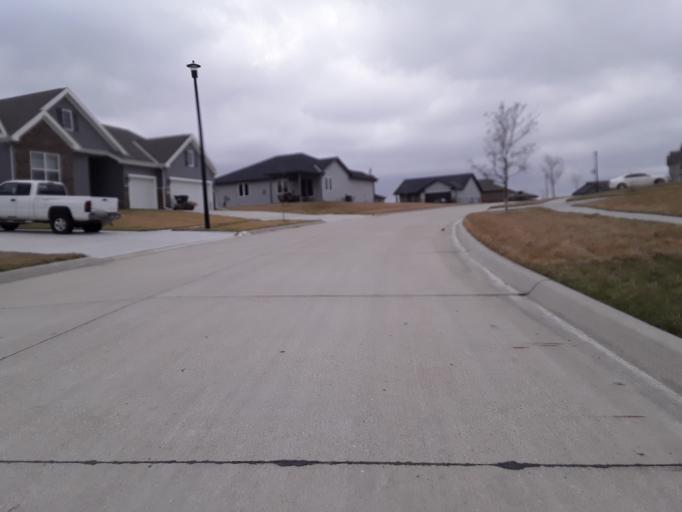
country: US
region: Nebraska
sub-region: Lancaster County
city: Lincoln
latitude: 40.8456
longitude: -96.5976
